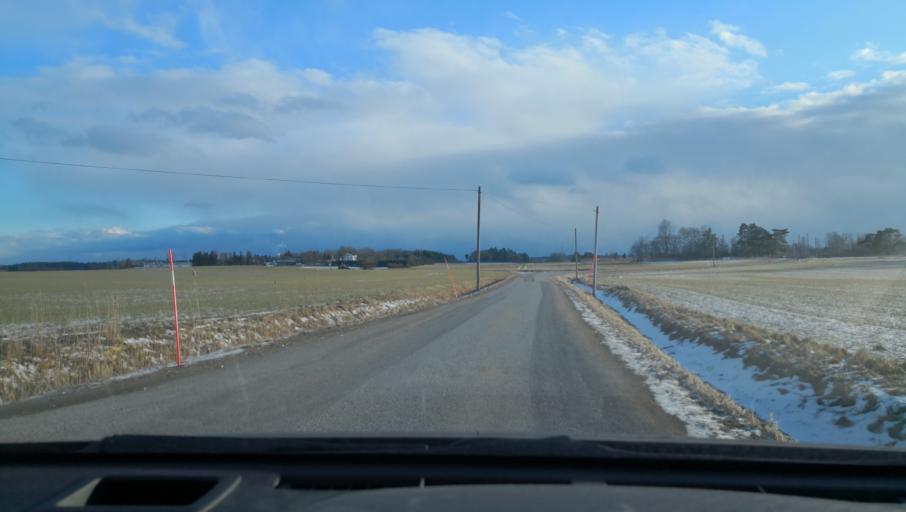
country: SE
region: Uppsala
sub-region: Enkopings Kommun
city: Irsta
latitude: 59.6900
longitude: 16.8594
